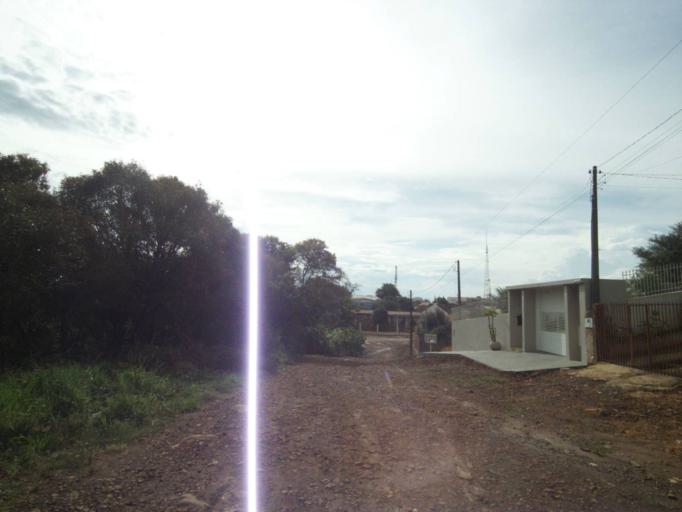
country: BR
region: Parana
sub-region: Guaraniacu
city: Guaraniacu
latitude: -25.1041
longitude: -52.8634
